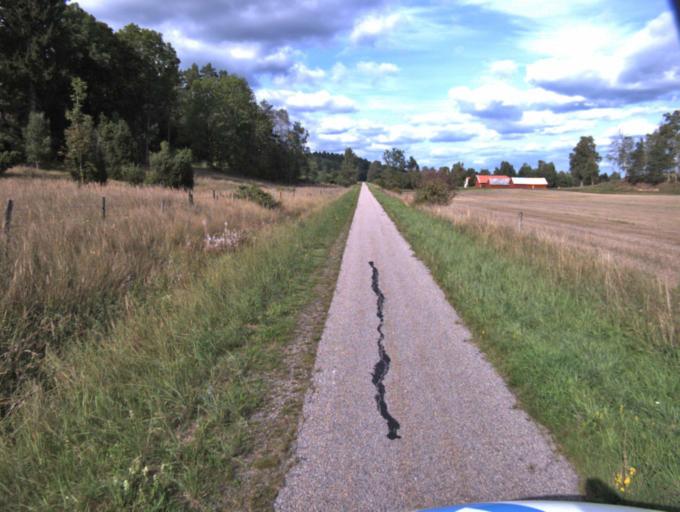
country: SE
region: Vaestra Goetaland
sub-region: Ulricehamns Kommun
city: Ulricehamn
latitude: 57.8817
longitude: 13.4309
